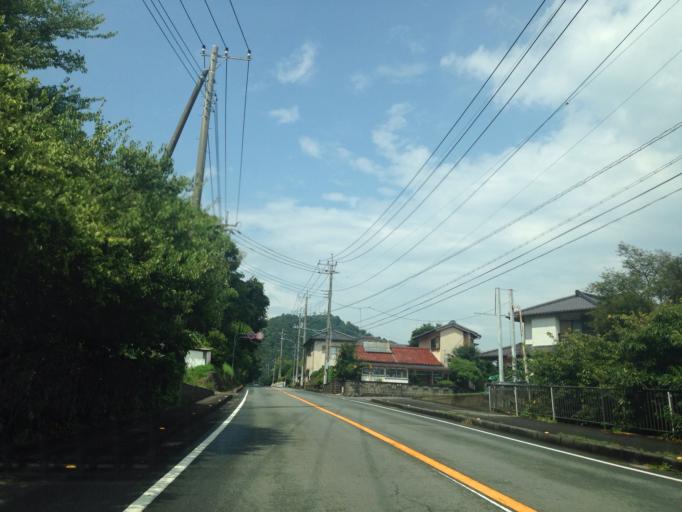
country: JP
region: Shizuoka
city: Ito
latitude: 34.9643
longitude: 138.9388
